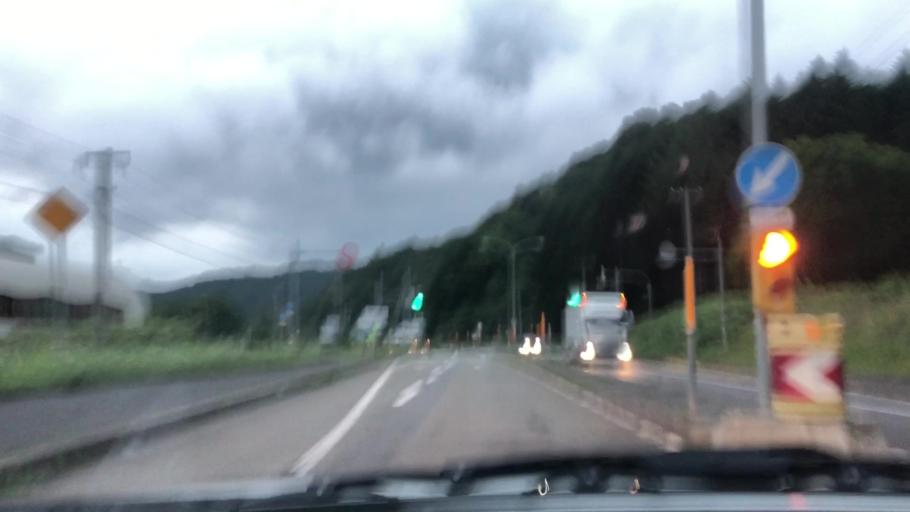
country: JP
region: Hokkaido
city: Chitose
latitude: 42.9121
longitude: 141.9727
